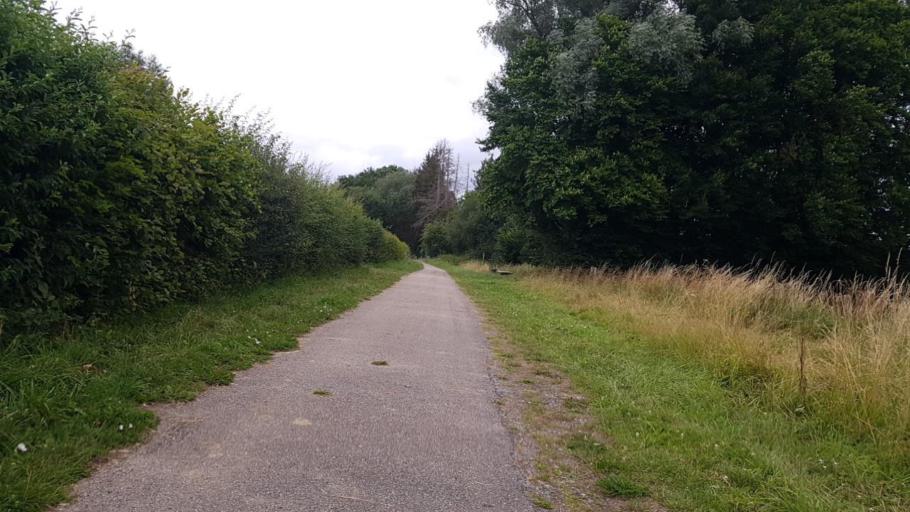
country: FR
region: Picardie
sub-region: Departement de l'Aisne
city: La Capelle
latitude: 49.9063
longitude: 3.9035
